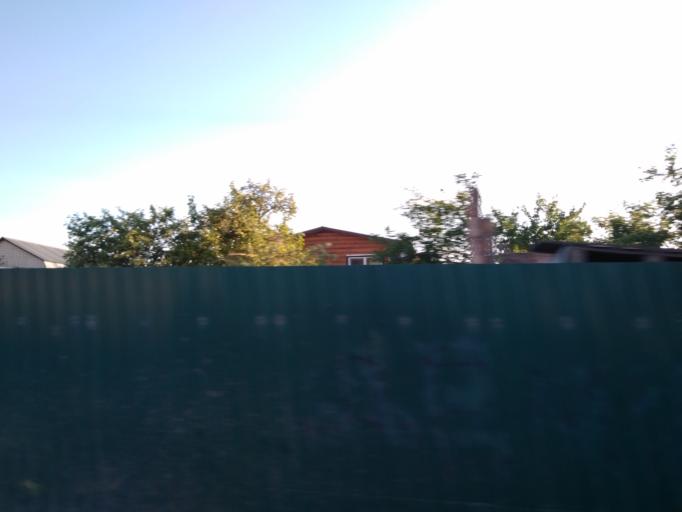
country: RU
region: Moskovskaya
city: Zhukovskiy
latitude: 55.5757
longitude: 38.1123
